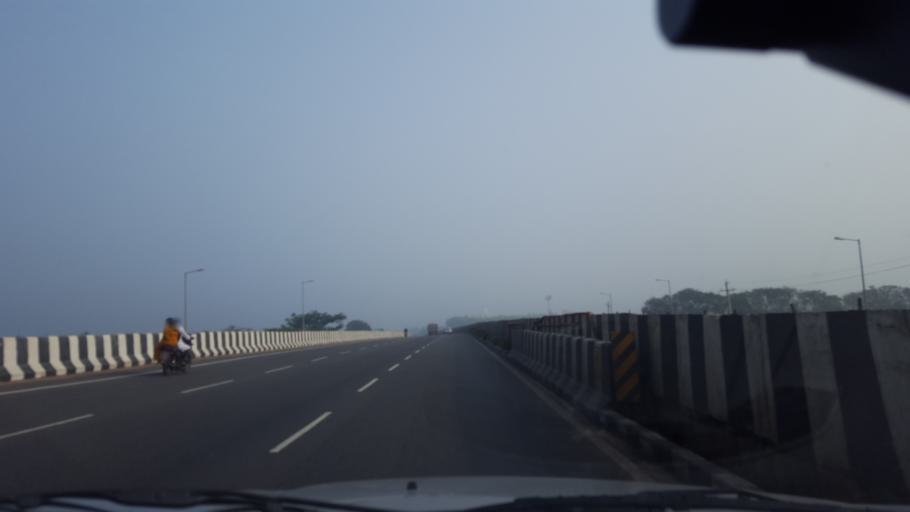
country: IN
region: Andhra Pradesh
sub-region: Prakasam
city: Ongole
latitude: 15.4248
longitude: 80.0403
